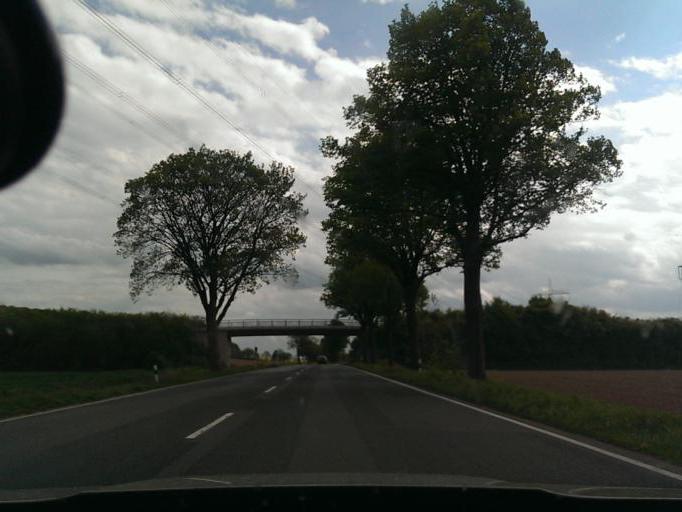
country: DE
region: Lower Saxony
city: Nordstemmen
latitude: 52.1790
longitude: 9.7460
